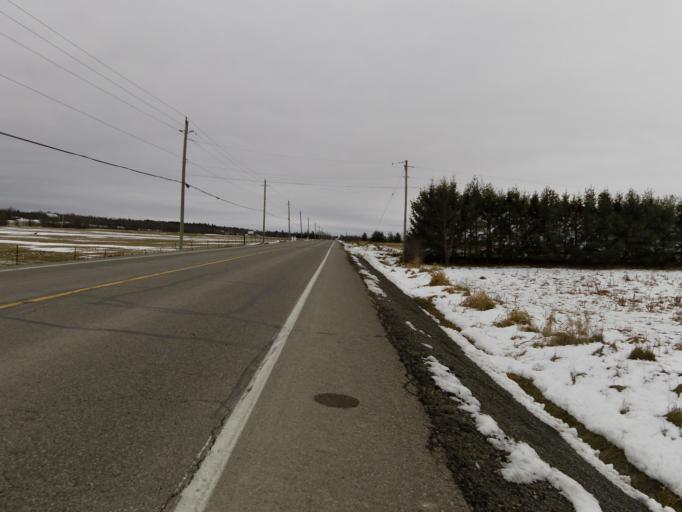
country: CA
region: Ontario
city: Carleton Place
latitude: 45.2601
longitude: -76.2326
